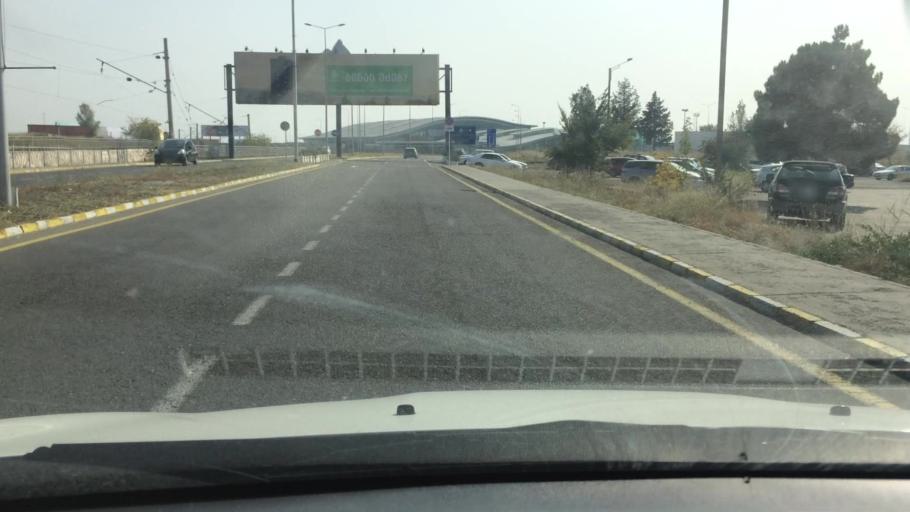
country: GE
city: Didi Lilo
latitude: 41.6736
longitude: 44.9622
